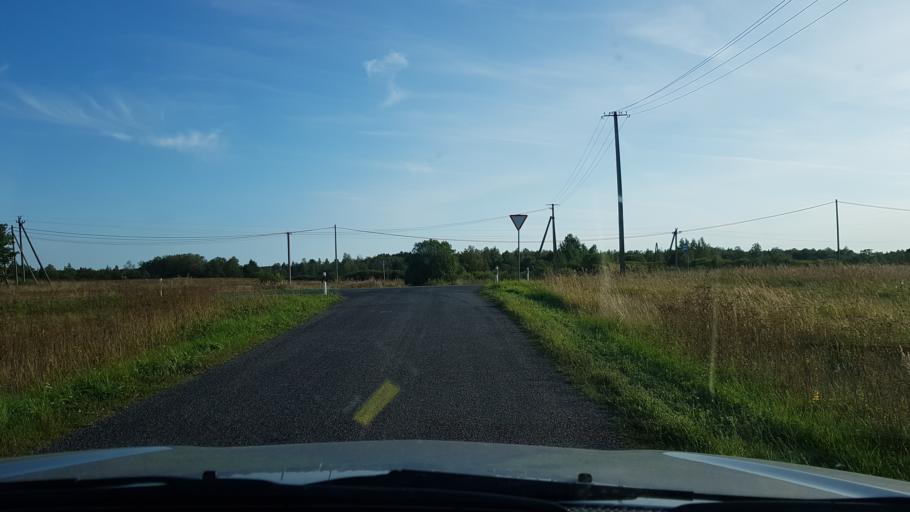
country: EE
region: Ida-Virumaa
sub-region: Narva-Joesuu linn
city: Narva-Joesuu
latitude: 59.3491
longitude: 28.0276
